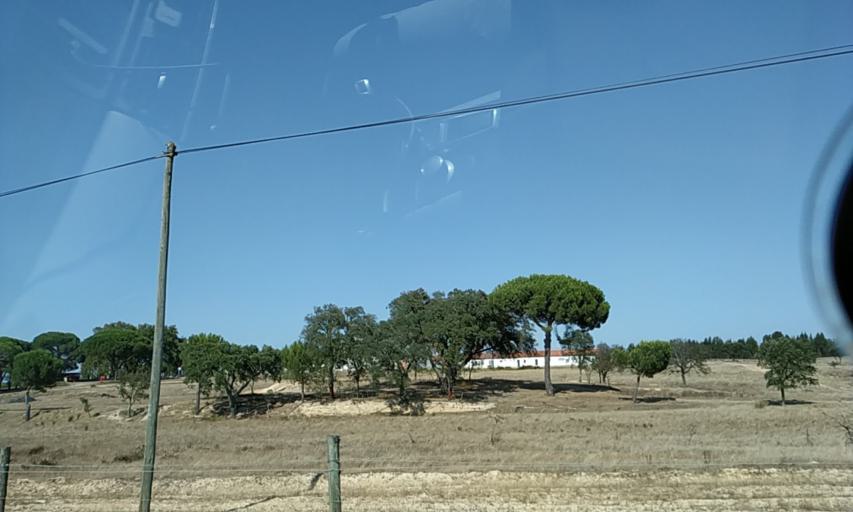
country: PT
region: Evora
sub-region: Vendas Novas
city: Vendas Novas
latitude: 38.7336
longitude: -8.6244
